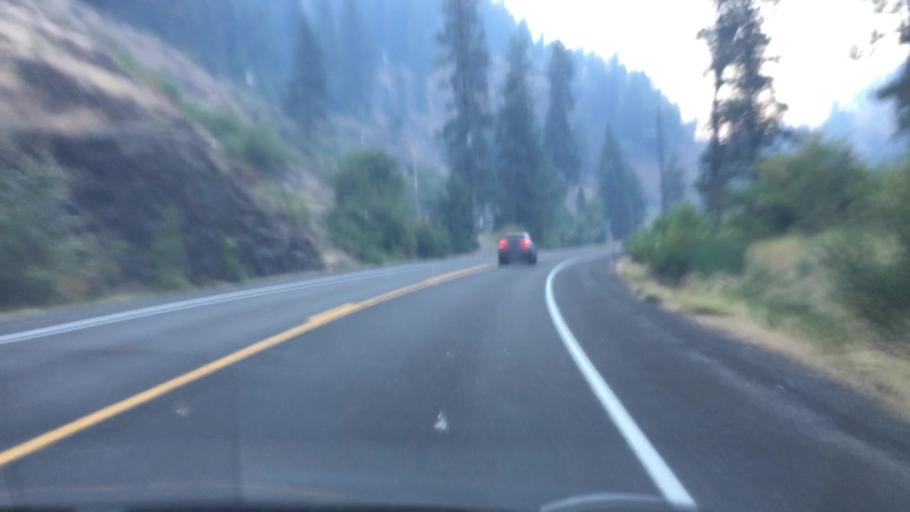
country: US
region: Idaho
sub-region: Valley County
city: McCall
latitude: 45.2304
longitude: -116.3254
